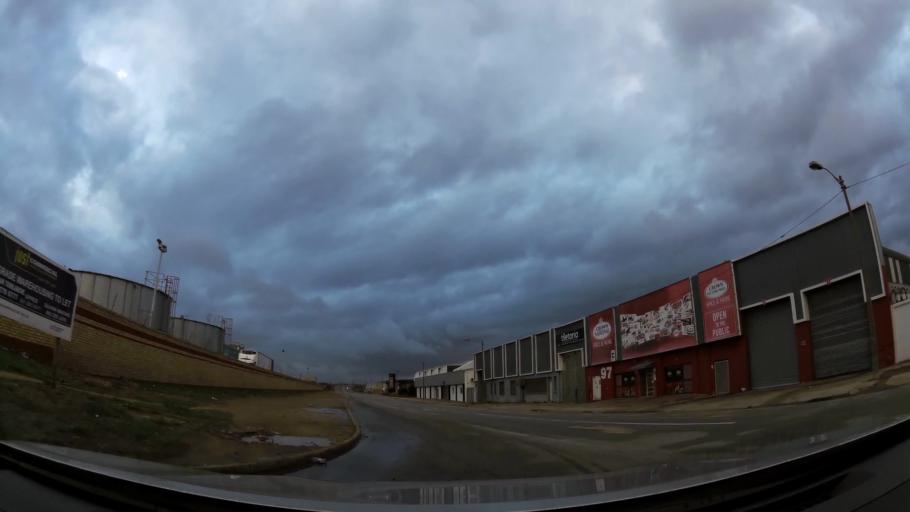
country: ZA
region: Eastern Cape
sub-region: Nelson Mandela Bay Metropolitan Municipality
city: Port Elizabeth
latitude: -33.9292
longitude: 25.6044
